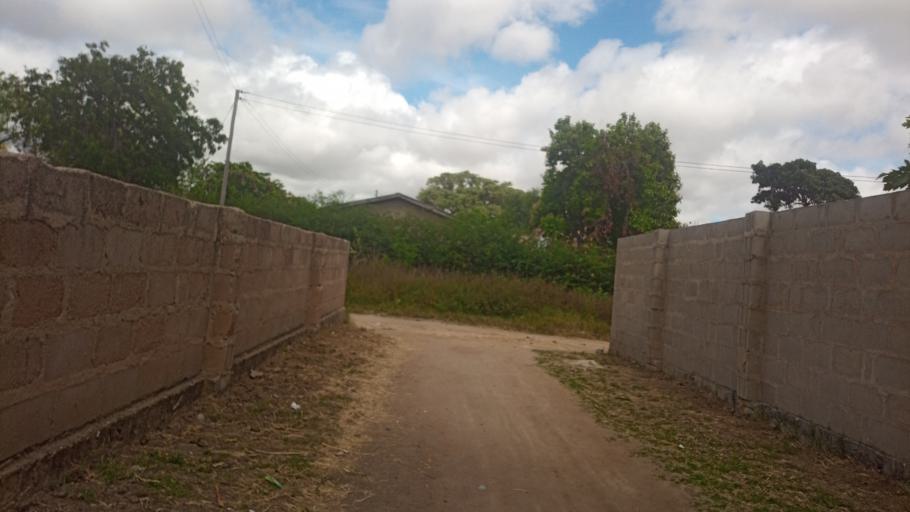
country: TZ
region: Dodoma
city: Dodoma
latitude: -6.1916
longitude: 35.7329
